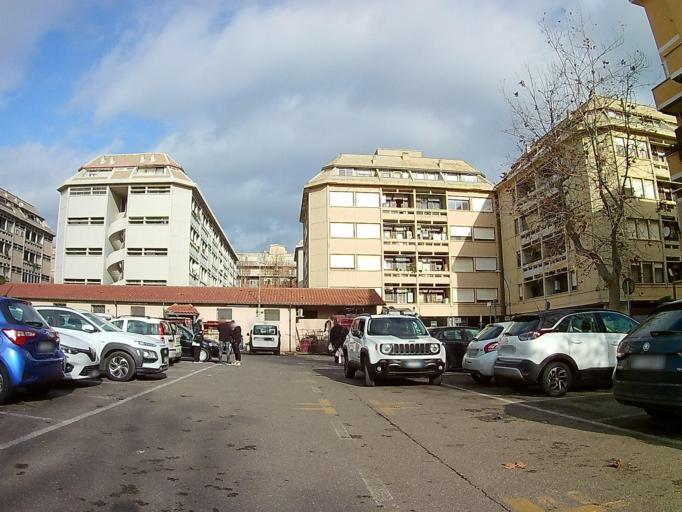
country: IT
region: Latium
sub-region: Citta metropolitana di Roma Capitale
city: Lido di Ostia
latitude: 41.7316
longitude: 12.2749
